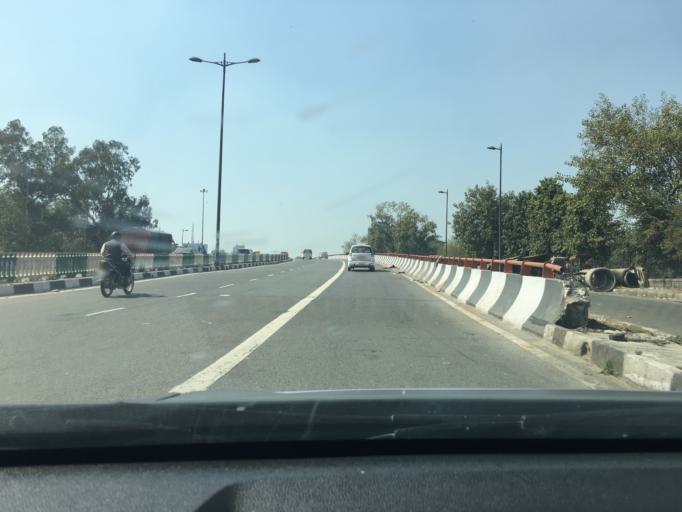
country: IN
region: NCT
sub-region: North Delhi
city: Delhi
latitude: 28.6611
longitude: 77.2410
